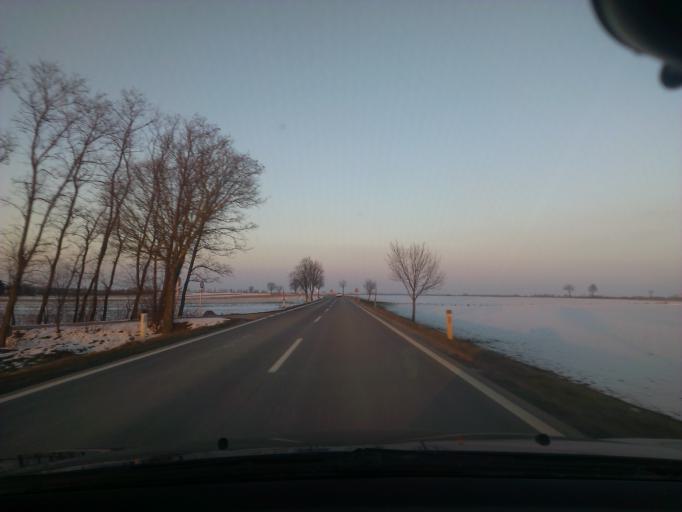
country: AT
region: Lower Austria
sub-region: Politischer Bezirk Baden
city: Seibersdorf
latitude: 47.9798
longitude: 16.5103
